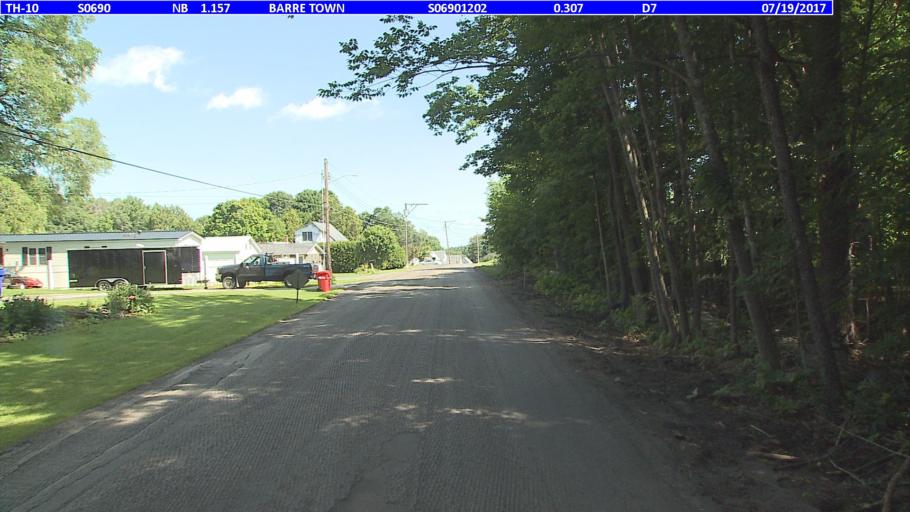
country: US
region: Vermont
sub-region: Washington County
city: South Barre
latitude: 44.1482
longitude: -72.4932
